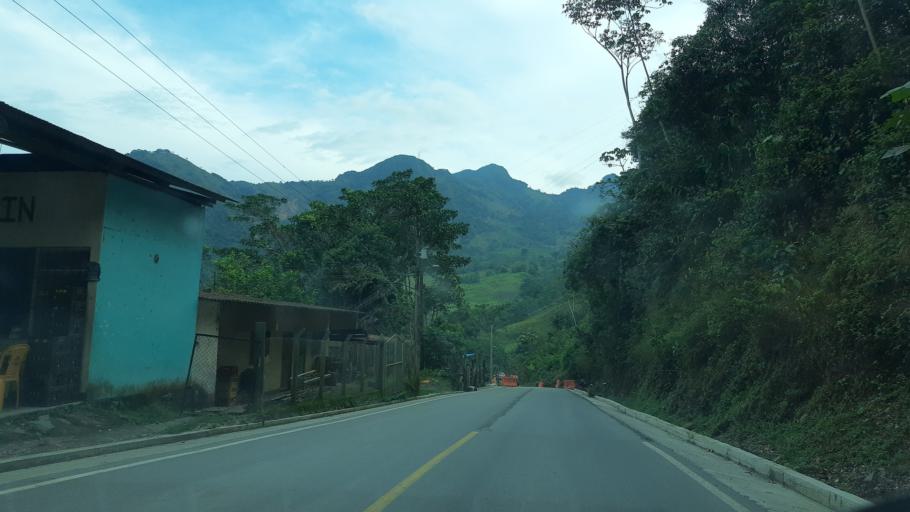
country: CO
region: Boyaca
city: Santa Maria
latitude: 4.8620
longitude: -73.2334
